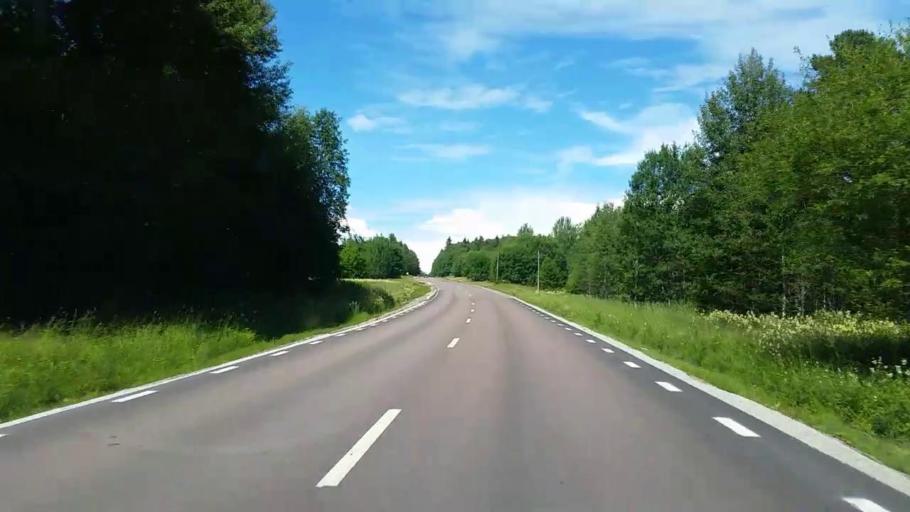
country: SE
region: Dalarna
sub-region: Rattviks Kommun
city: Raettvik
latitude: 61.0127
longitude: 15.2163
